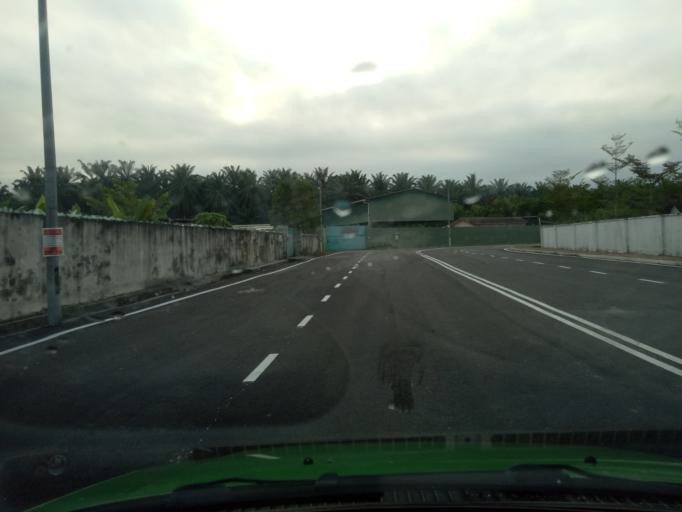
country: MY
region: Selangor
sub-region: Hulu Langat
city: Semenyih
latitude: 2.9323
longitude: 101.8678
